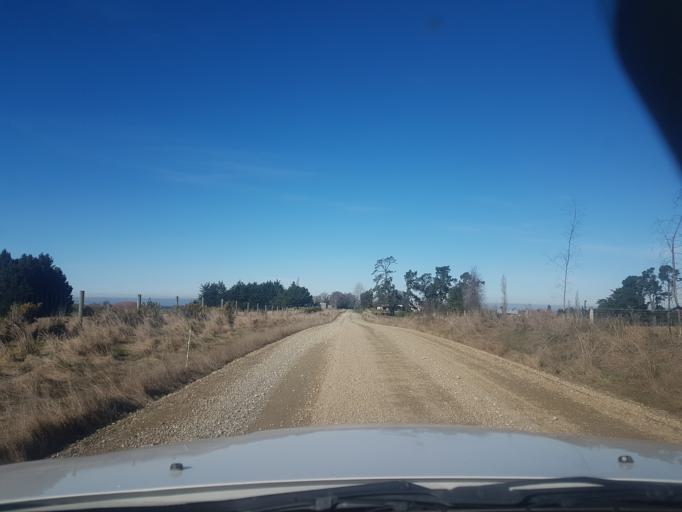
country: NZ
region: Canterbury
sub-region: Timaru District
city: Pleasant Point
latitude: -44.3709
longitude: 171.0745
